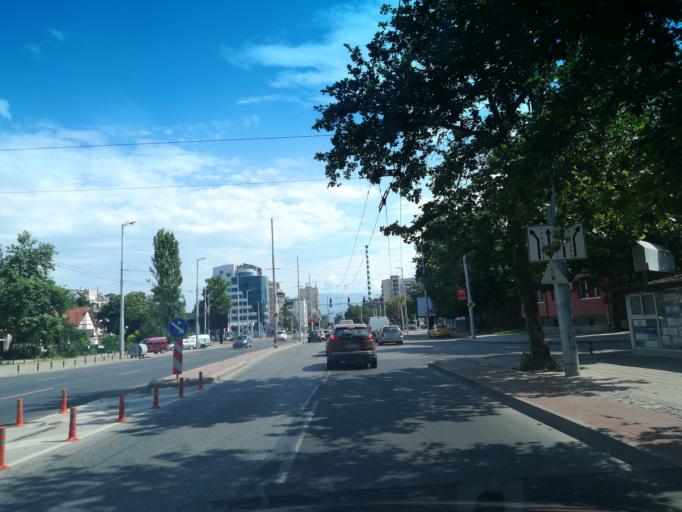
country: BG
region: Plovdiv
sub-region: Obshtina Plovdiv
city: Plovdiv
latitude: 42.1482
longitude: 24.7631
